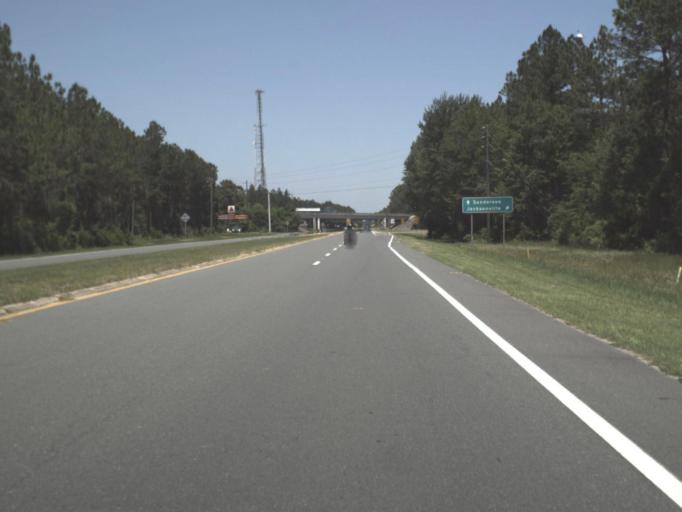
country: US
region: Florida
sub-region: Baker County
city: Macclenny
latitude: 30.2373
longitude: -82.3082
